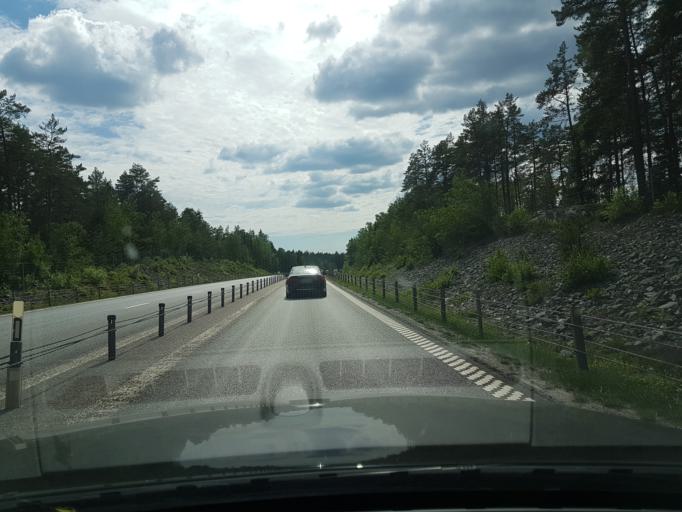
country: SE
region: Stockholm
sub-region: Norrtalje Kommun
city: Rimbo
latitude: 59.6233
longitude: 18.3078
